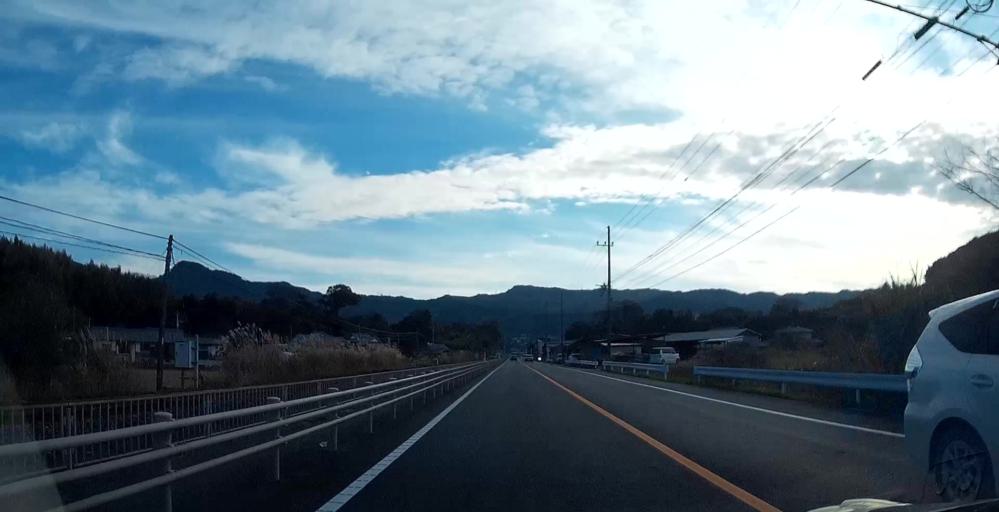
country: JP
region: Kumamoto
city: Uto
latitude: 32.6765
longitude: 130.5532
